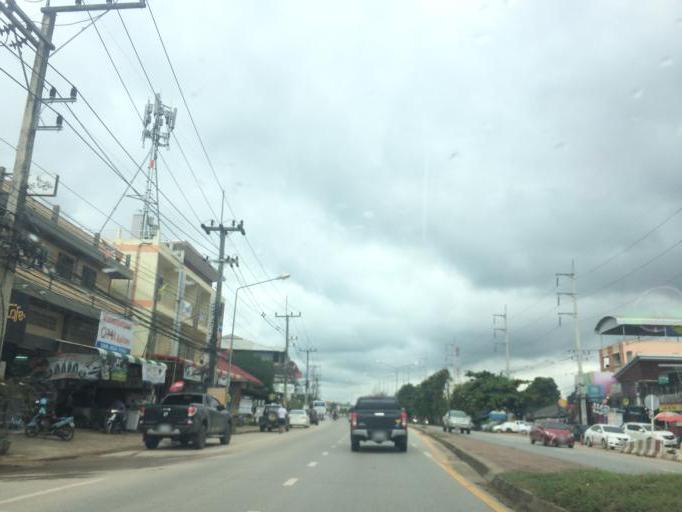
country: TH
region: Chiang Rai
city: Mae Chan
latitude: 20.0491
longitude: 99.8760
